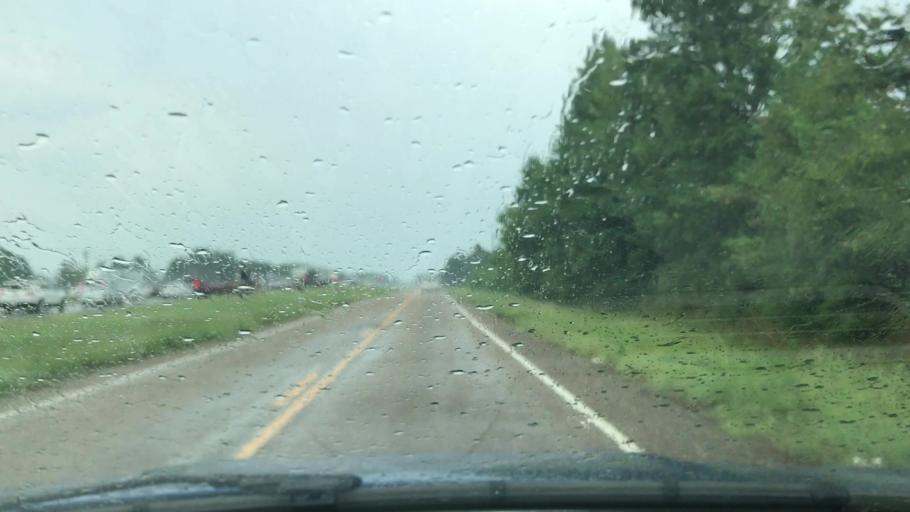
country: US
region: Texas
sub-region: Harrison County
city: Waskom
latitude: 32.4887
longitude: -94.1398
